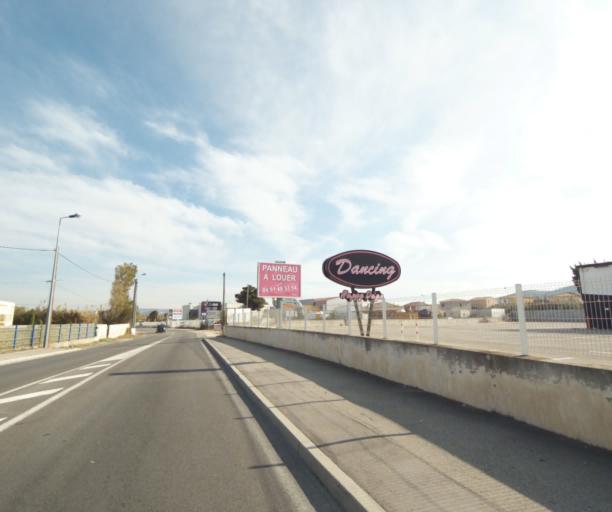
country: FR
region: Provence-Alpes-Cote d'Azur
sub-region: Departement des Bouches-du-Rhone
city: Chateauneuf-les-Martigues
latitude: 43.3902
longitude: 5.1631
